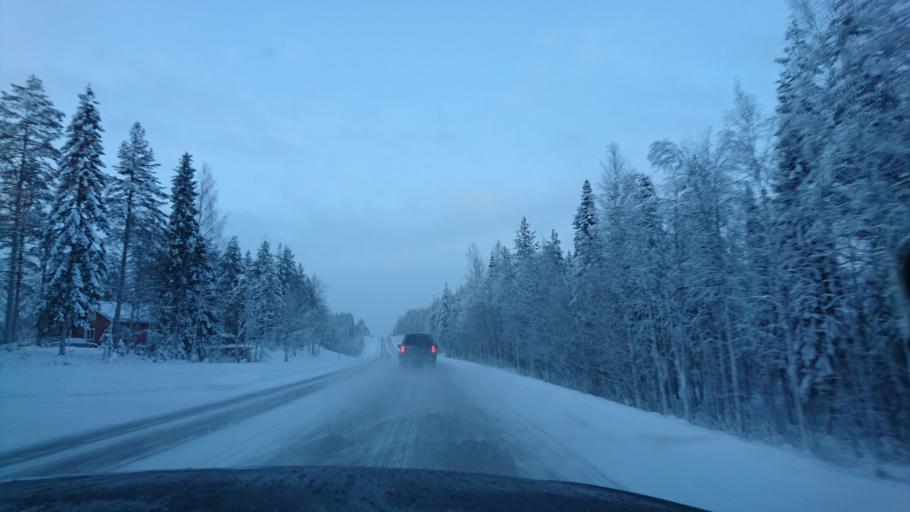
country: FI
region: Northern Ostrobothnia
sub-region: Koillismaa
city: Taivalkoski
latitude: 65.4689
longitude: 27.6931
